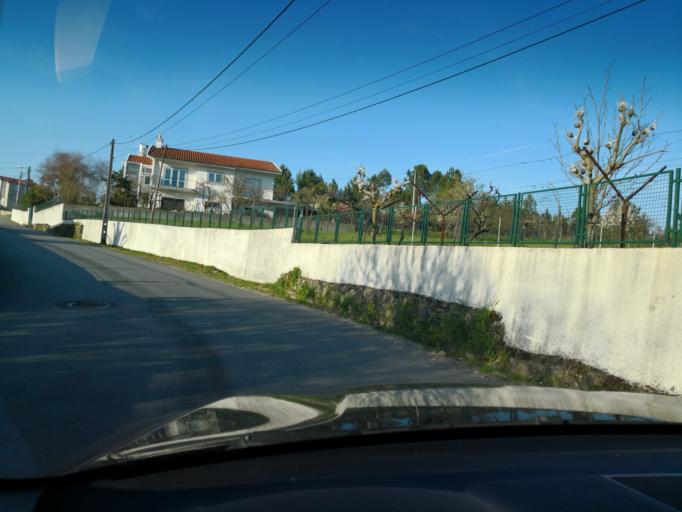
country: PT
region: Vila Real
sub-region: Vila Real
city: Vila Real
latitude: 41.2947
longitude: -7.7660
